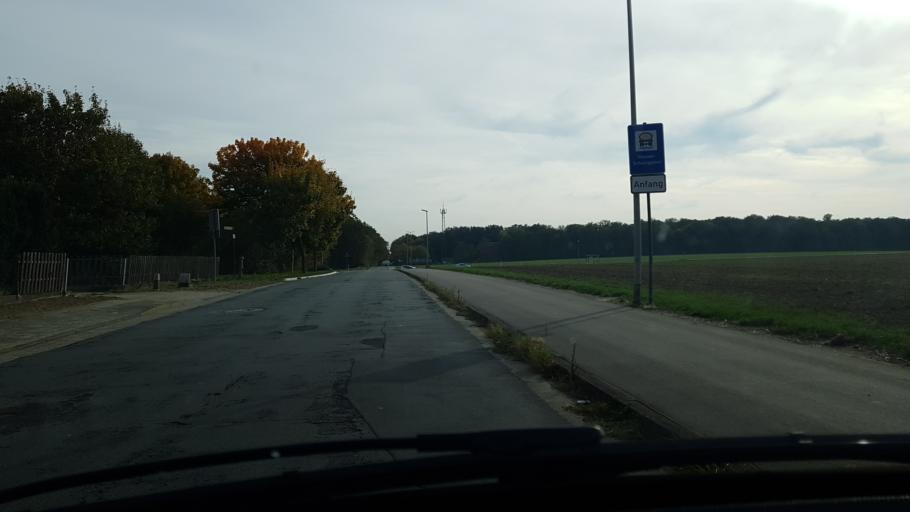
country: DE
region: Lower Saxony
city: Lehre
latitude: 52.3707
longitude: 10.6723
